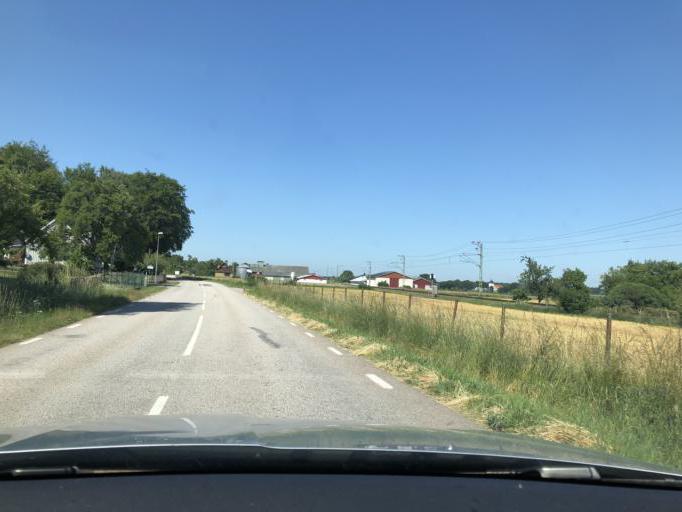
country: SE
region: Blekinge
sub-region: Solvesborgs Kommun
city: Soelvesborg
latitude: 56.0977
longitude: 14.6166
